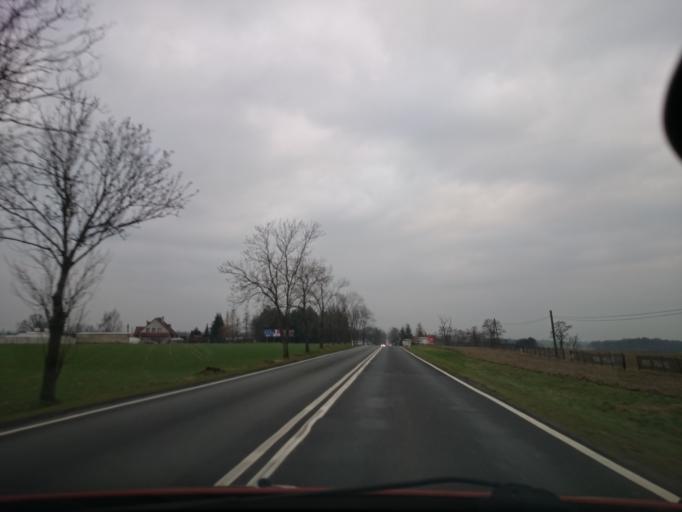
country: PL
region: Opole Voivodeship
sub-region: Powiat nyski
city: Pakoslawice
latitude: 50.5346
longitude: 17.3651
